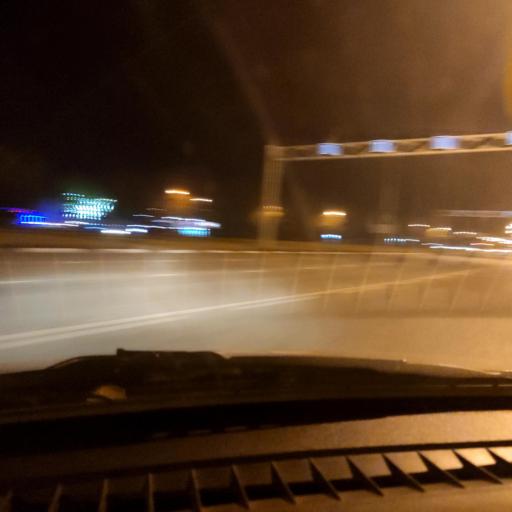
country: RU
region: Samara
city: Tol'yatti
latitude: 53.5211
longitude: 49.2600
